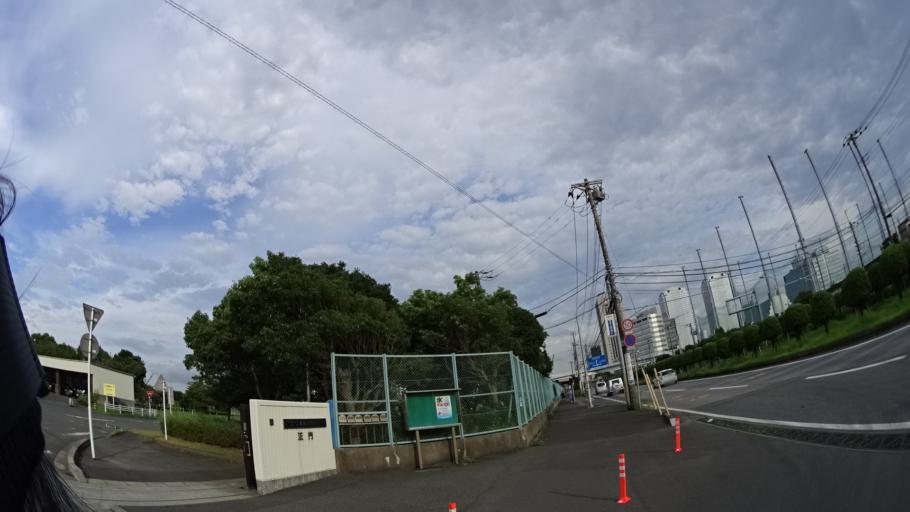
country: JP
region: Chiba
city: Funabashi
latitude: 35.6552
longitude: 140.0342
